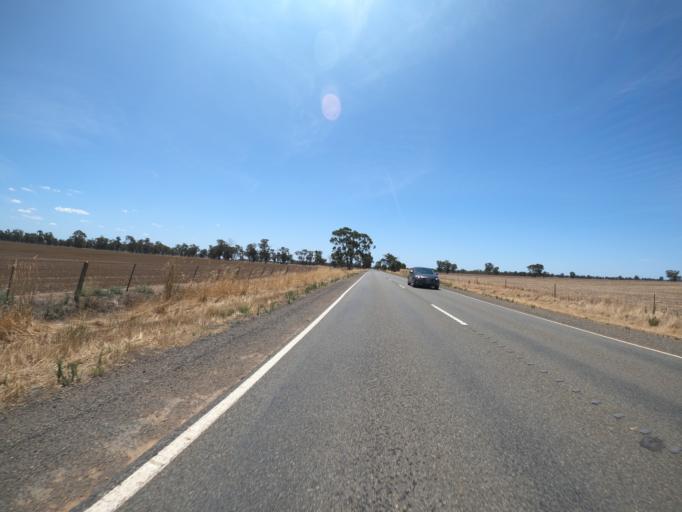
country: AU
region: Victoria
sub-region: Moira
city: Yarrawonga
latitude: -36.1733
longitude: 145.9672
